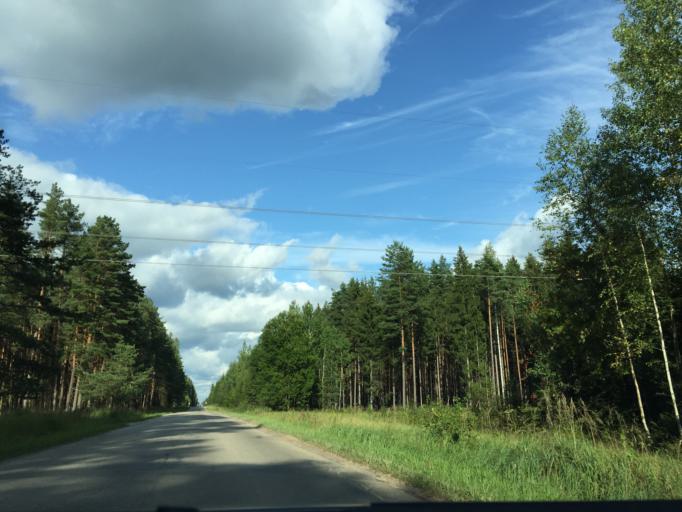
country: LV
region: Ogre
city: Ogre
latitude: 56.8322
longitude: 24.6507
